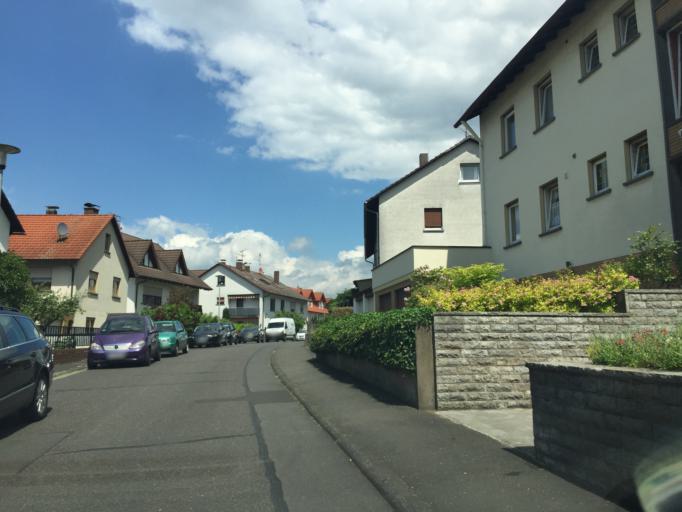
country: DE
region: Bavaria
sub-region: Regierungsbezirk Unterfranken
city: Goldbach
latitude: 49.9877
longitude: 9.1779
